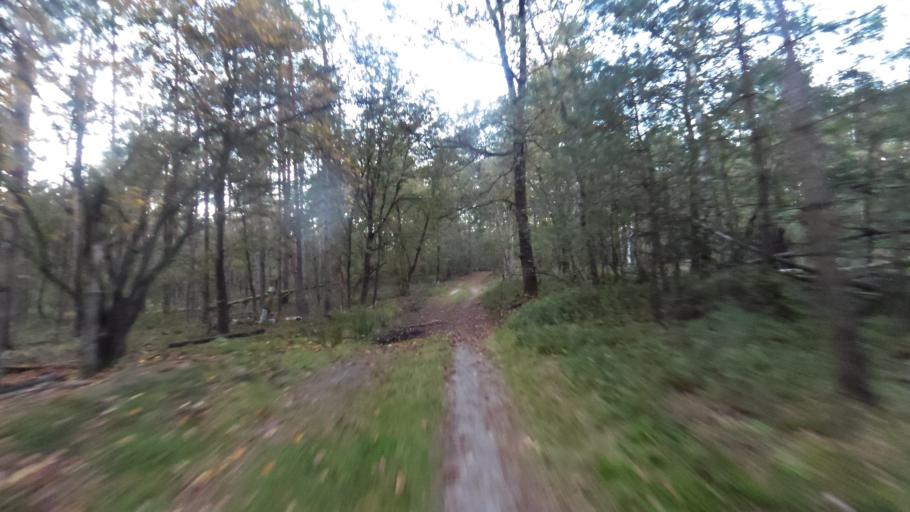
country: NL
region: Gelderland
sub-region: Gemeente Nunspeet
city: Nunspeet
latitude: 52.3332
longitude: 5.8008
